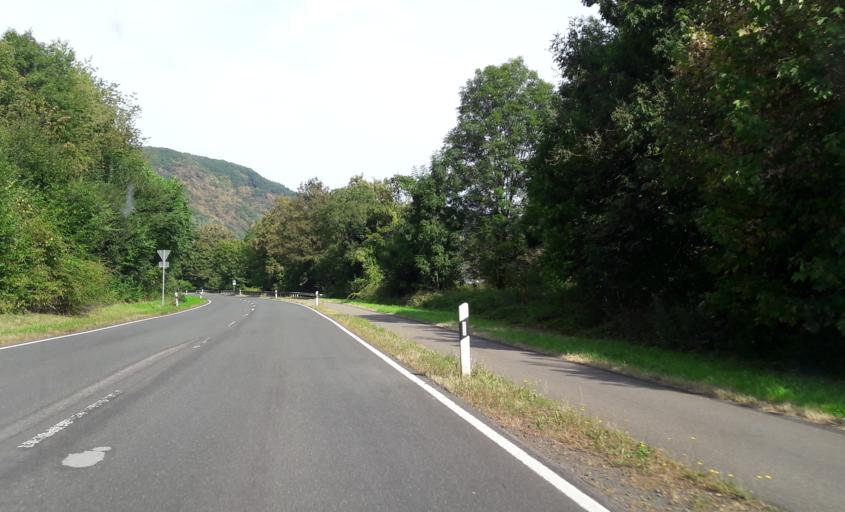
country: DE
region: Rheinland-Pfalz
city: Nehren
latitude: 50.0913
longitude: 7.1970
